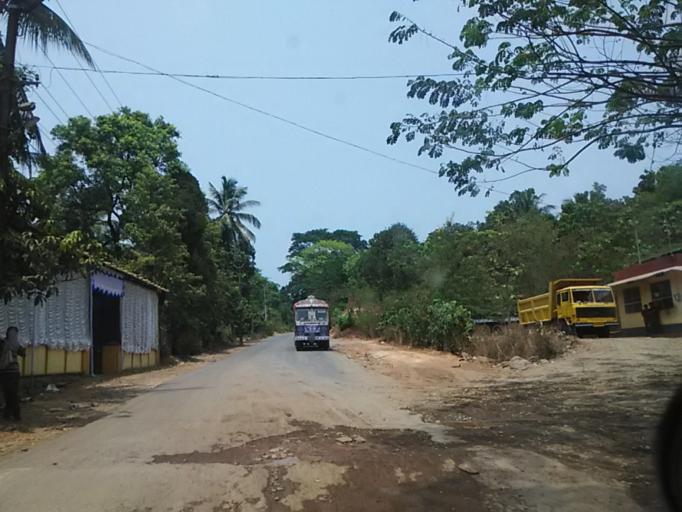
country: IN
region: Karnataka
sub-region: Kodagu
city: Virarajendrapet
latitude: 12.0523
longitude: 75.7160
